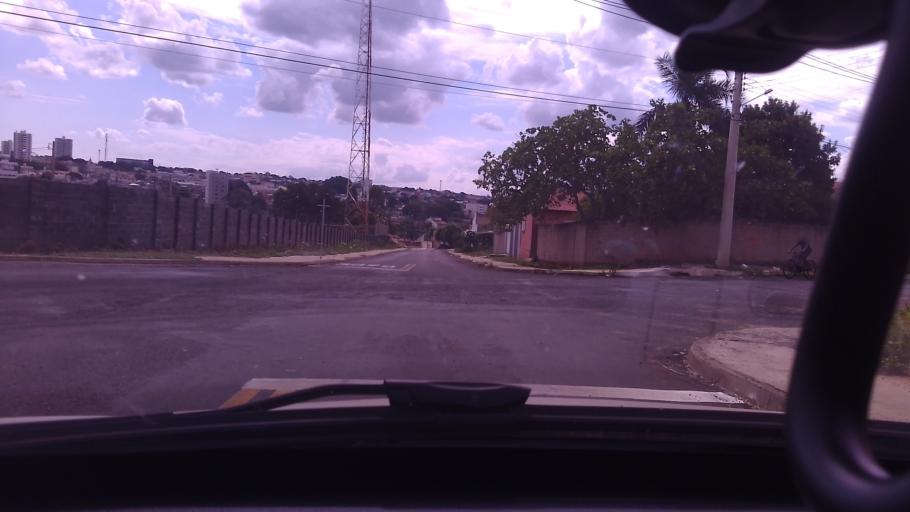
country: BR
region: Goias
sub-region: Mineiros
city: Mineiros
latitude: -17.5768
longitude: -52.5522
